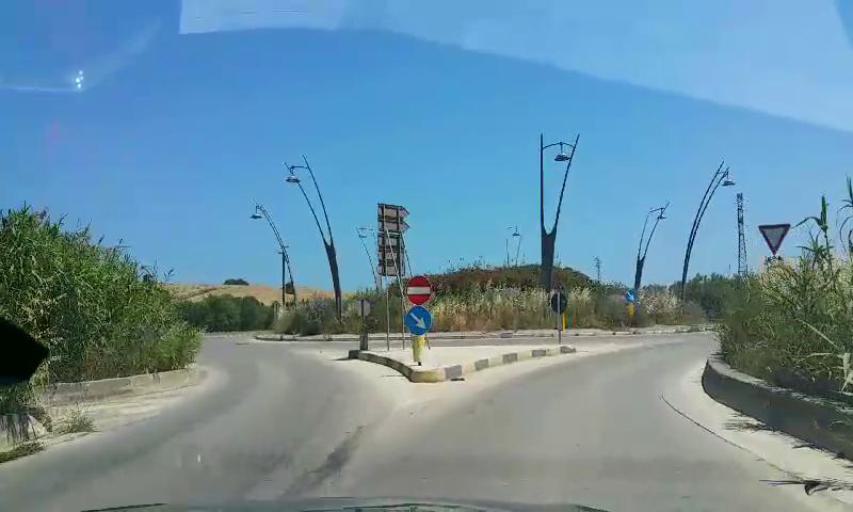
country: IT
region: Molise
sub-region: Provincia di Campobasso
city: San Giacomo degli Schiavoni
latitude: 41.9965
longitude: 14.9518
